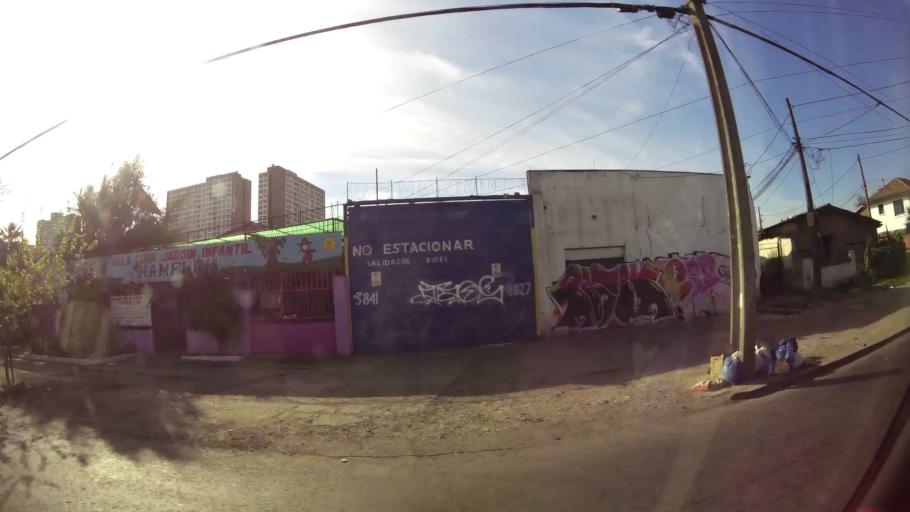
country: CL
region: Santiago Metropolitan
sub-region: Provincia de Santiago
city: Santiago
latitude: -33.4571
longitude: -70.6870
